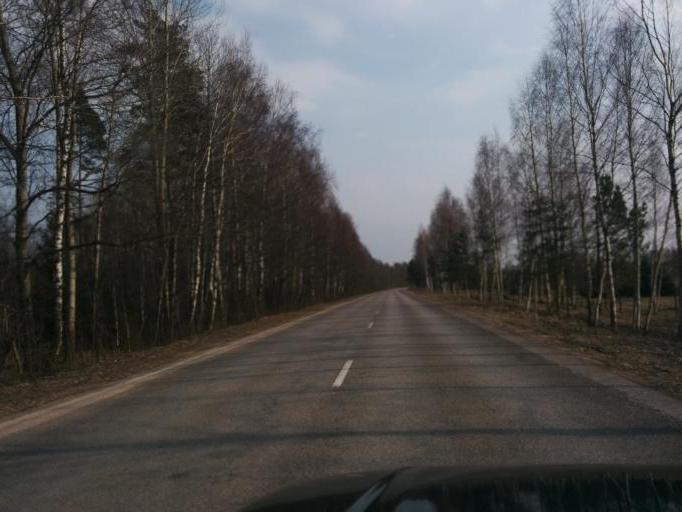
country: LV
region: Kekava
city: Balozi
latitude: 56.7793
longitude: 24.1042
